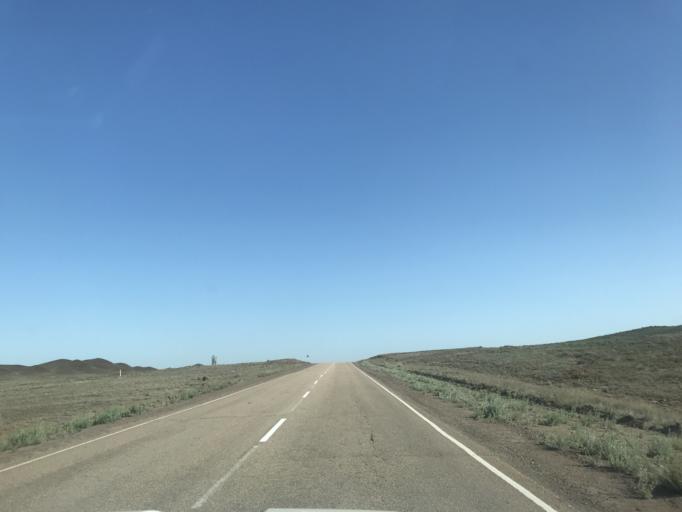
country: KZ
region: Zhambyl
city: Mynaral
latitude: 45.4091
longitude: 73.6311
